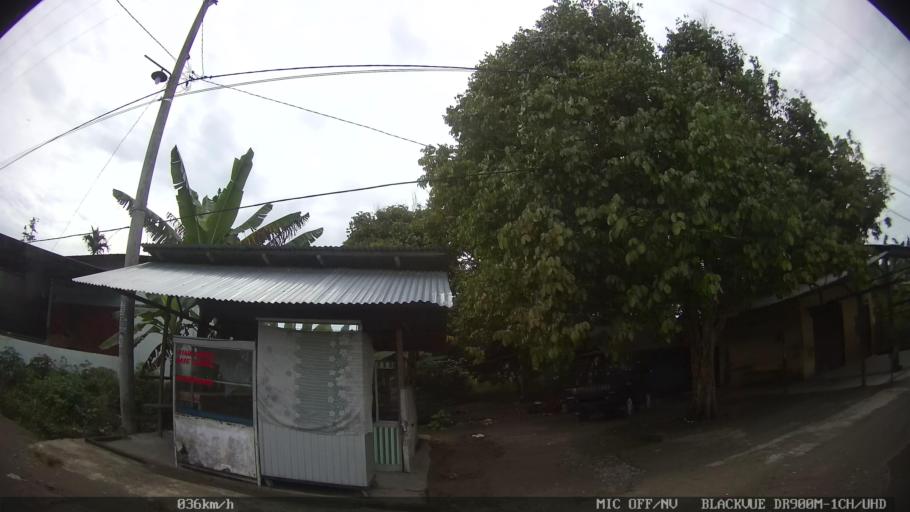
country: ID
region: North Sumatra
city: Sunggal
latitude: 3.5769
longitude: 98.5648
